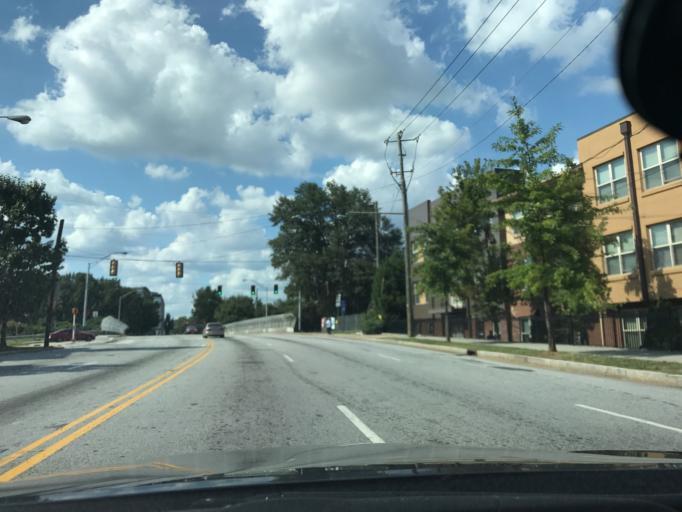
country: US
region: Georgia
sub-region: Fulton County
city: Atlanta
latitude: 33.7416
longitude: -84.4029
